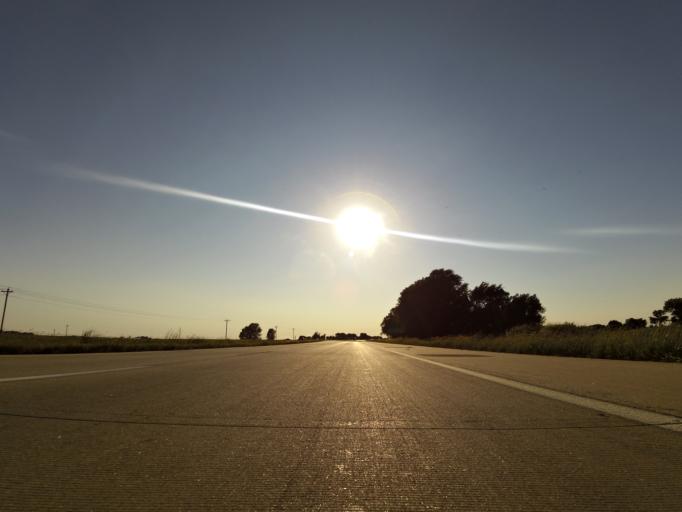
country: US
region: Kansas
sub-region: Sedgwick County
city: Colwich
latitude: 37.8251
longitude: -97.5342
